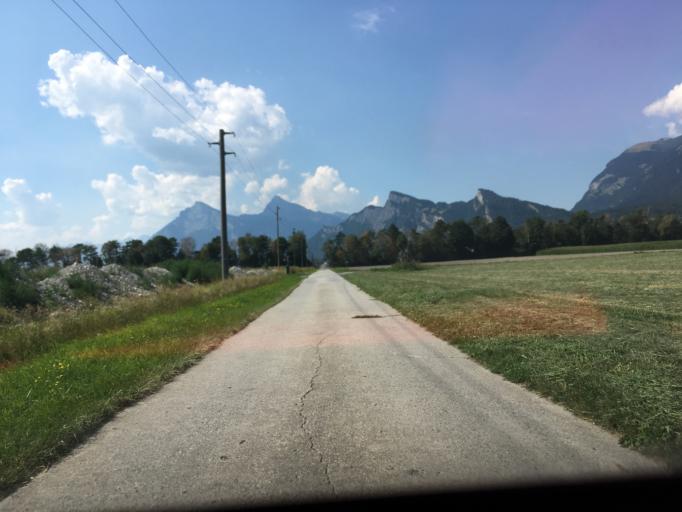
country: CH
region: Grisons
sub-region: Landquart District
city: Maienfeld
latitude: 46.9930
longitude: 9.5358
